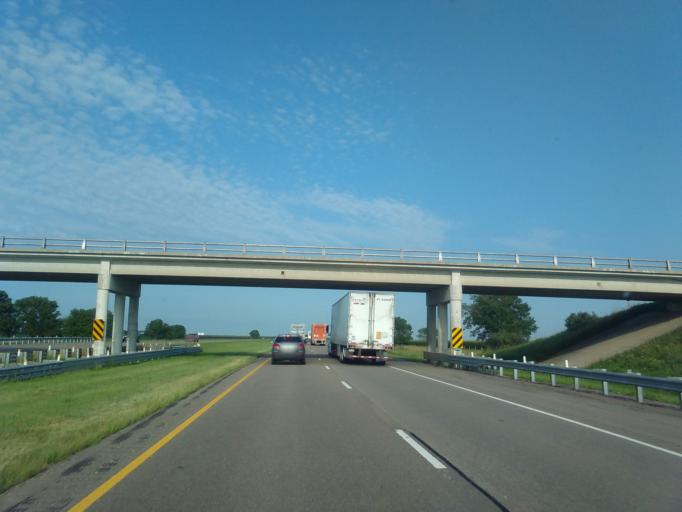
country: US
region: Nebraska
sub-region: York County
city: York
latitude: 40.8218
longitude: -97.7505
